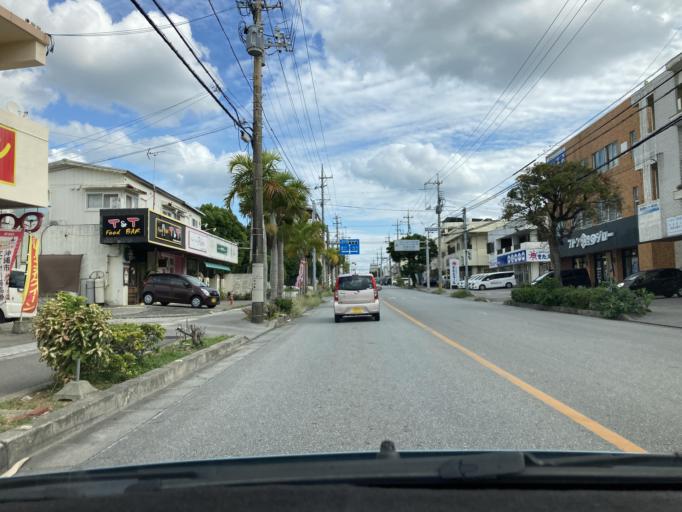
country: JP
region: Okinawa
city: Okinawa
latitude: 26.3606
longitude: 127.8192
